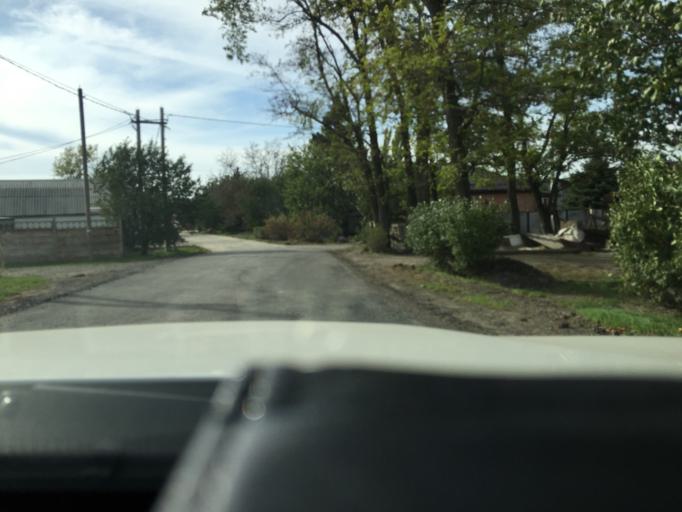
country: RU
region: Rostov
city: Aksay
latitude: 47.3025
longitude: 39.8312
